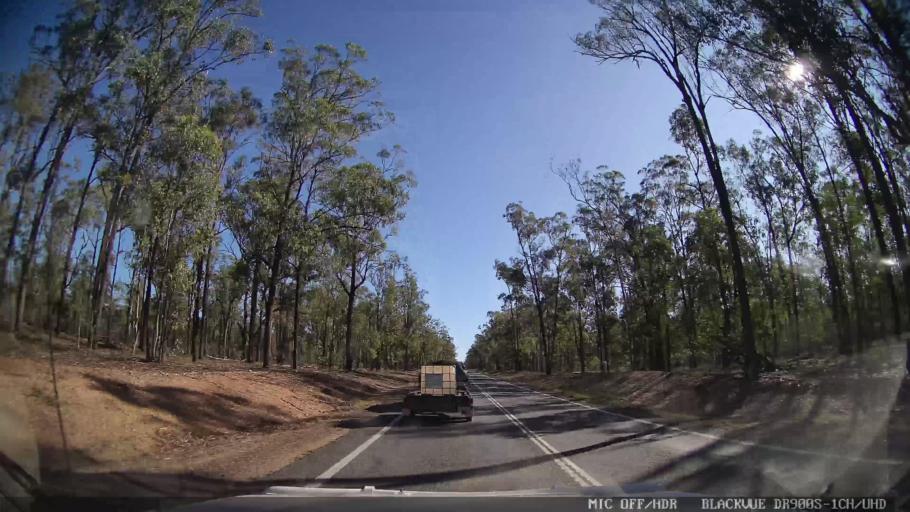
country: AU
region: Queensland
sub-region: Bundaberg
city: Childers
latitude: -25.2159
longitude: 152.0762
